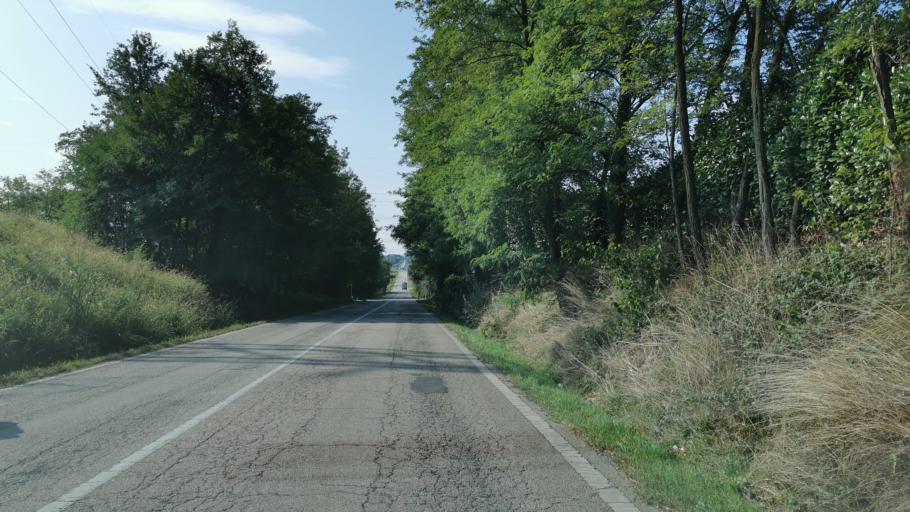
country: IT
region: Piedmont
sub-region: Provincia di Torino
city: Lombardore
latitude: 45.2089
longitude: 7.7291
